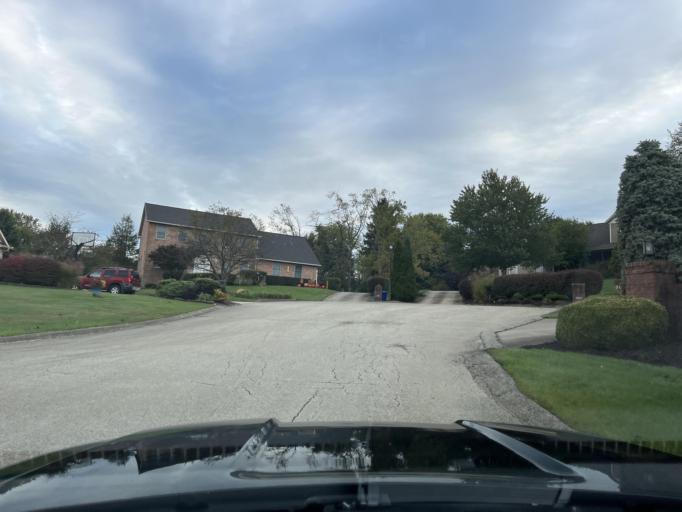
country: US
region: Pennsylvania
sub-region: Fayette County
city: Leith-Hatfield
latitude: 39.8762
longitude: -79.7297
